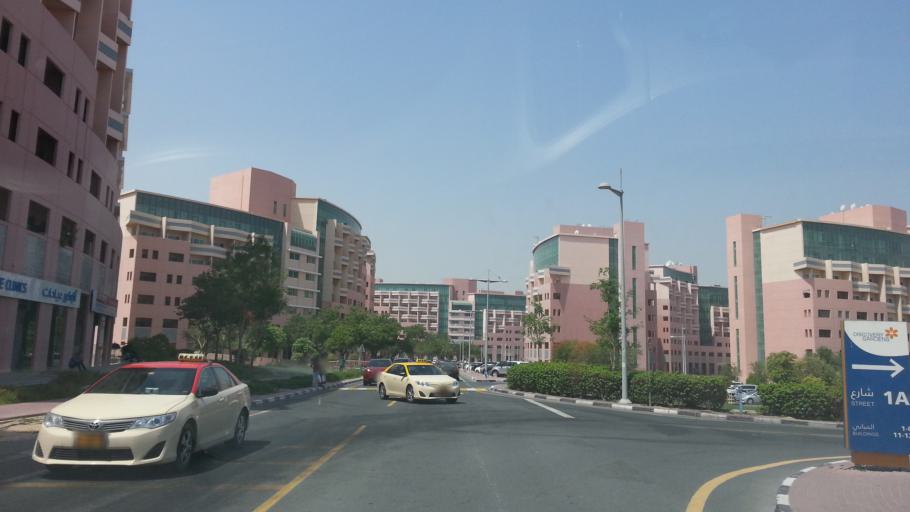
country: AE
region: Dubai
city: Dubai
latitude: 25.0506
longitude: 55.1329
